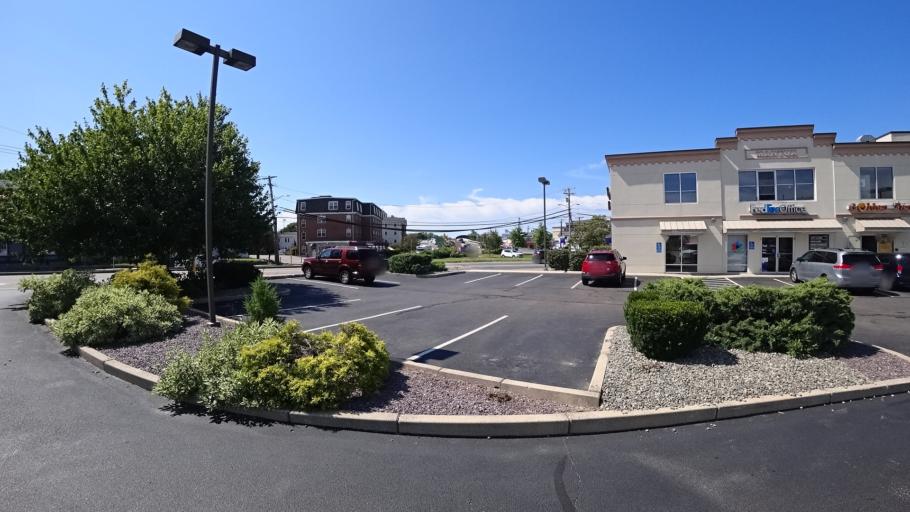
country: US
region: Massachusetts
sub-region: Norfolk County
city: Dedham
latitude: 42.2507
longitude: -71.1709
